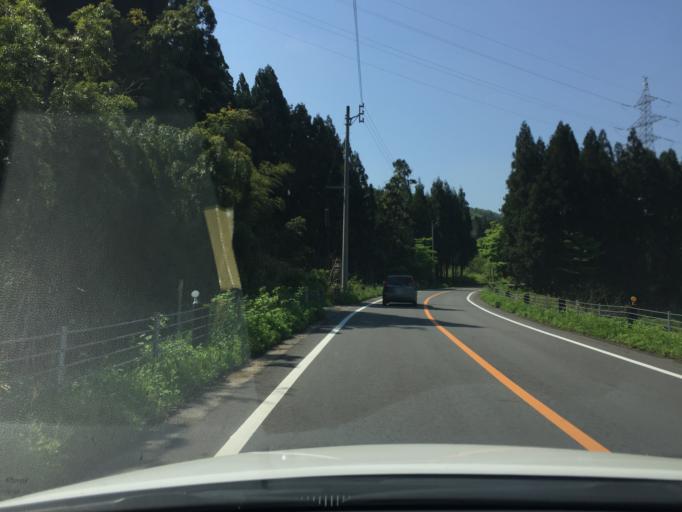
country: JP
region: Niigata
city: Muramatsu
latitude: 37.6593
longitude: 139.1385
